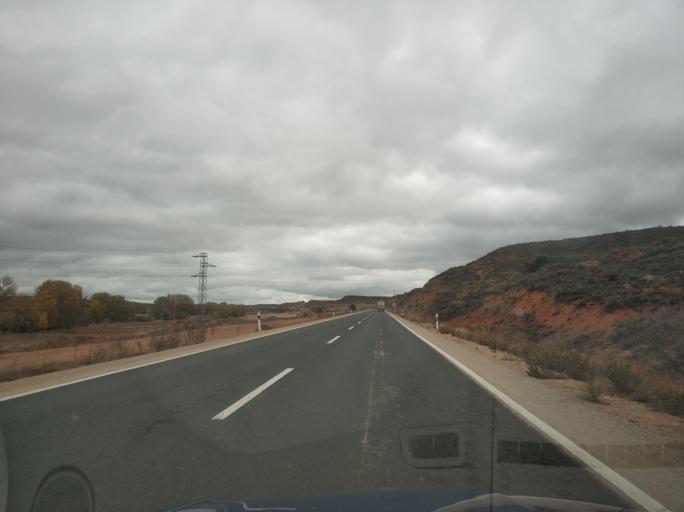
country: ES
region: Castille and Leon
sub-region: Provincia de Soria
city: San Esteban de Gormaz
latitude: 41.5797
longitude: -3.2249
